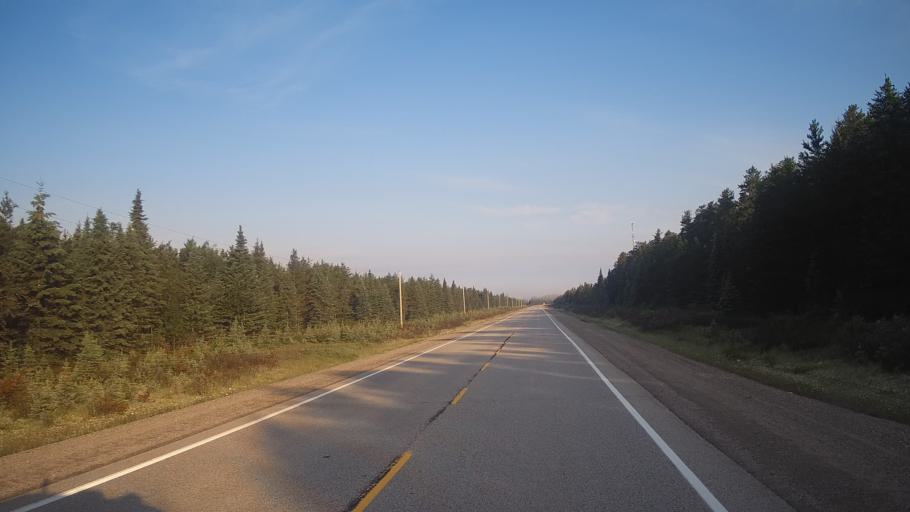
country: CA
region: Ontario
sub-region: Rainy River District
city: Atikokan
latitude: 49.3281
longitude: -91.4273
